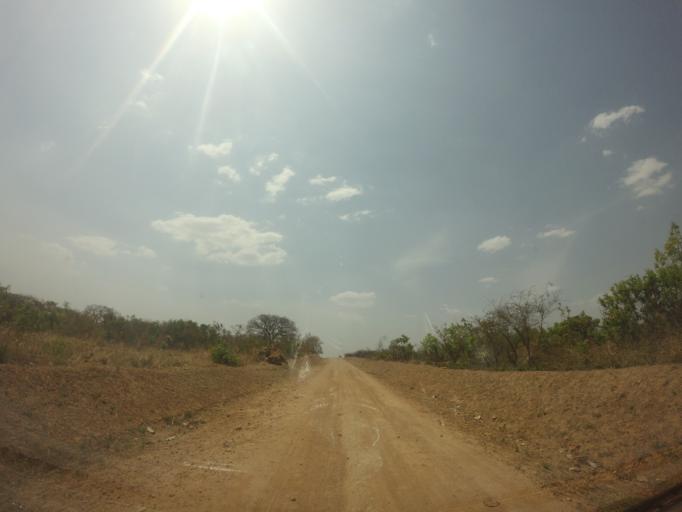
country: UG
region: Northern Region
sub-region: Arua District
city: Arua
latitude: 2.8971
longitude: 31.1271
